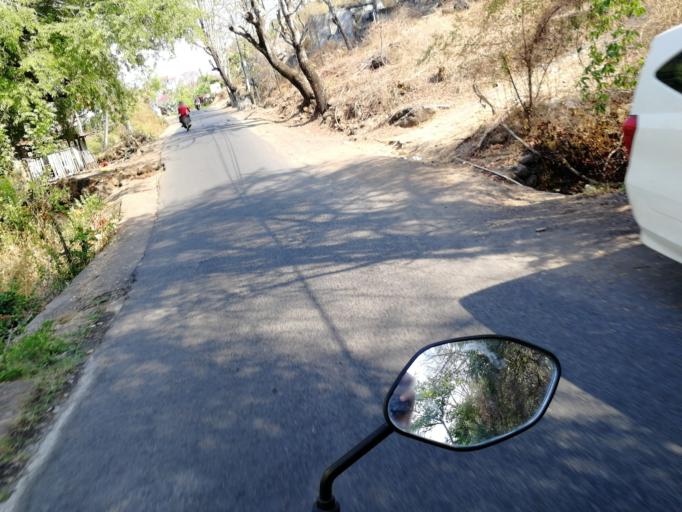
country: ID
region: Bali
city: Biaslantang Kaler
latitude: -8.3418
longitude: 115.6668
